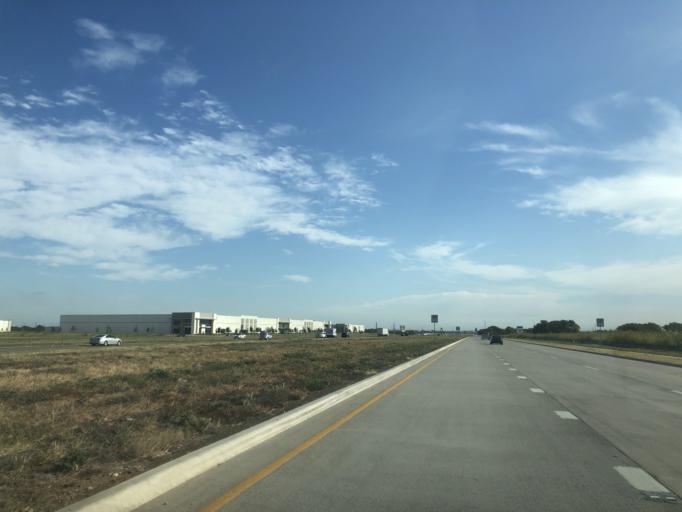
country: US
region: Texas
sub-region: Denton County
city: Roanoke
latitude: 33.0051
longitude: -97.2890
